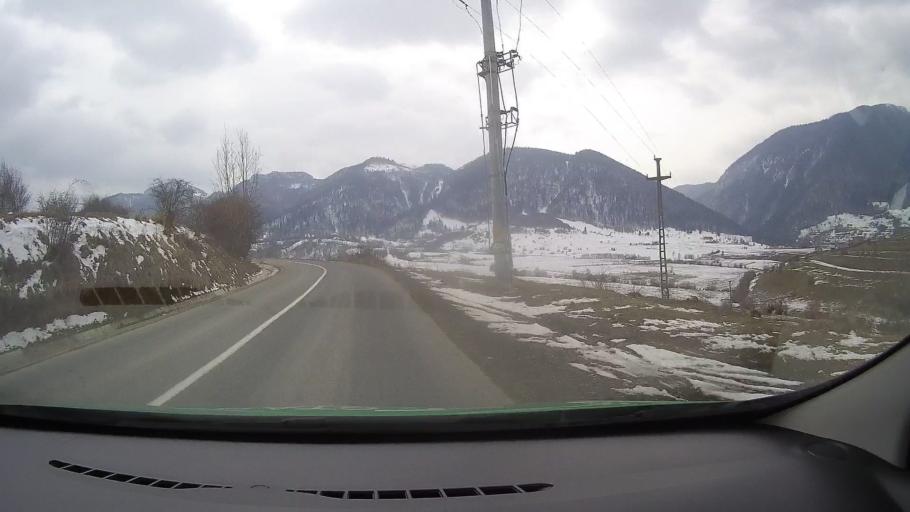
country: RO
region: Brasov
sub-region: Comuna Zarnesti
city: Zarnesti
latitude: 45.5525
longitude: 25.3196
